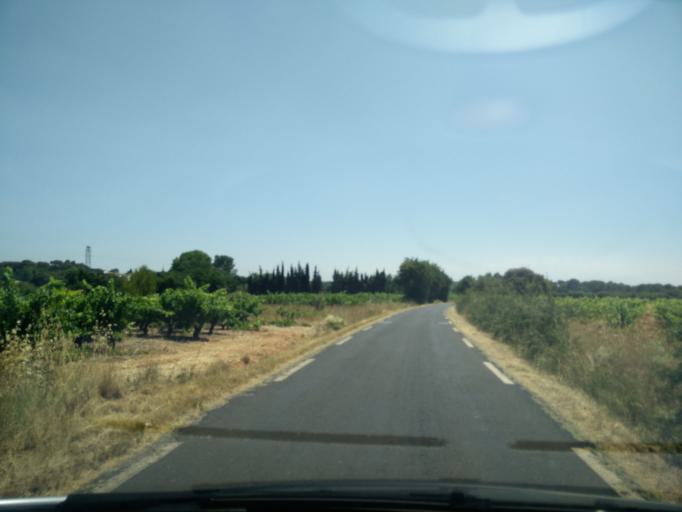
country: FR
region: Languedoc-Roussillon
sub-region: Departement de l'Herault
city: Saint-Christol
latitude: 43.7212
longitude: 4.0927
